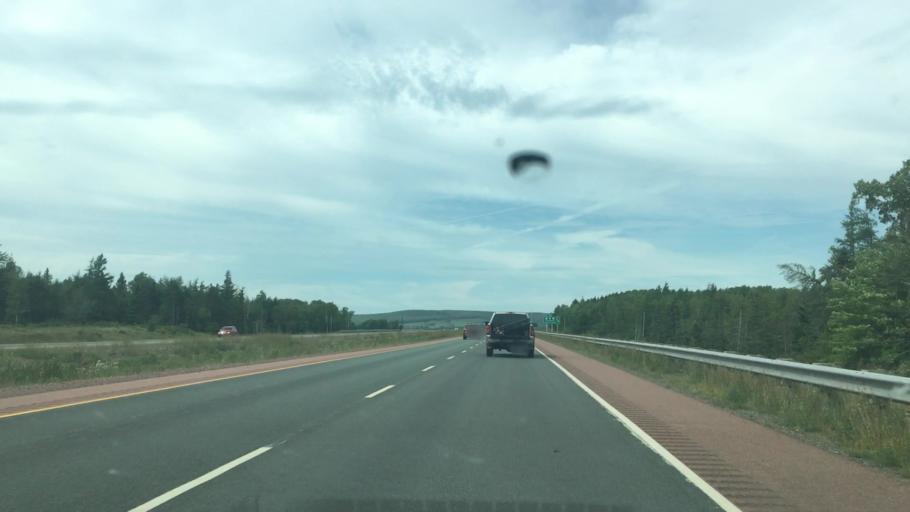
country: CA
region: Nova Scotia
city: Antigonish
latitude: 45.6094
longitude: -61.9875
